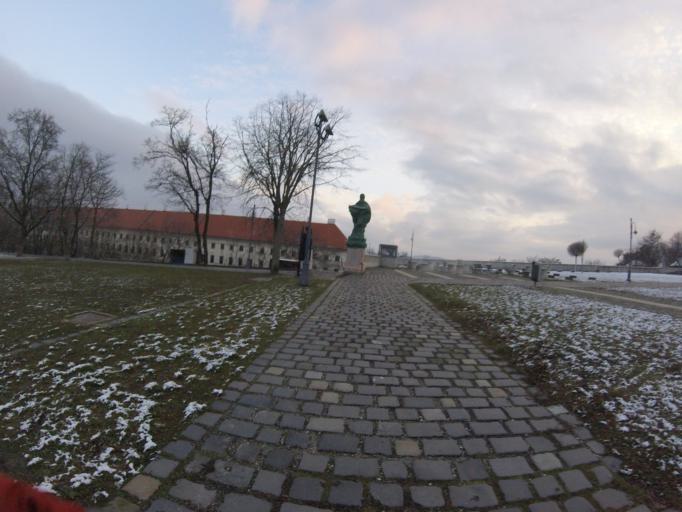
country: HU
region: Komarom-Esztergom
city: Esztergom
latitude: 47.7997
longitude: 18.7383
